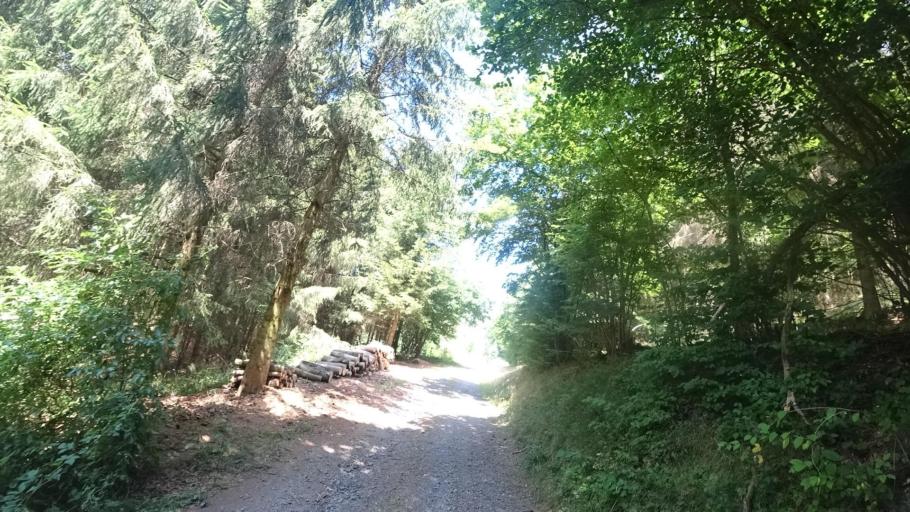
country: DE
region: Rheinland-Pfalz
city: Heckenbach
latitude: 50.4882
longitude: 7.0871
